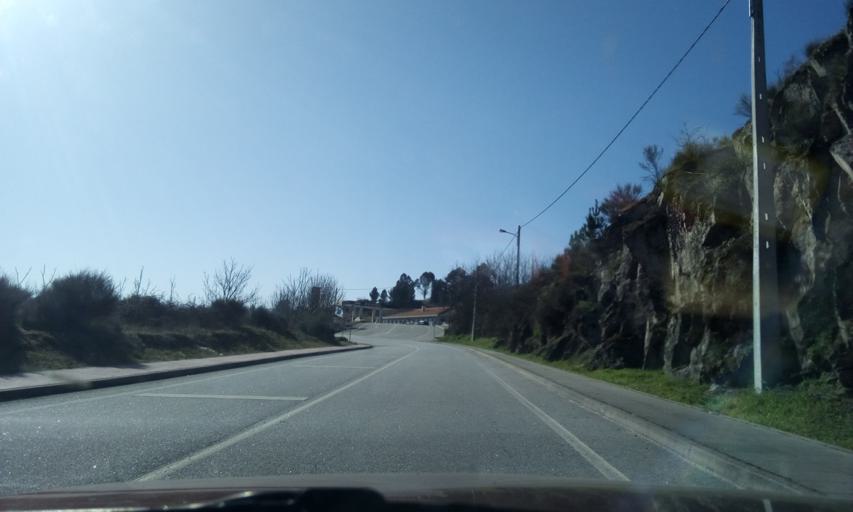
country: PT
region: Guarda
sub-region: Celorico da Beira
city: Celorico da Beira
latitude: 40.6530
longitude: -7.3836
